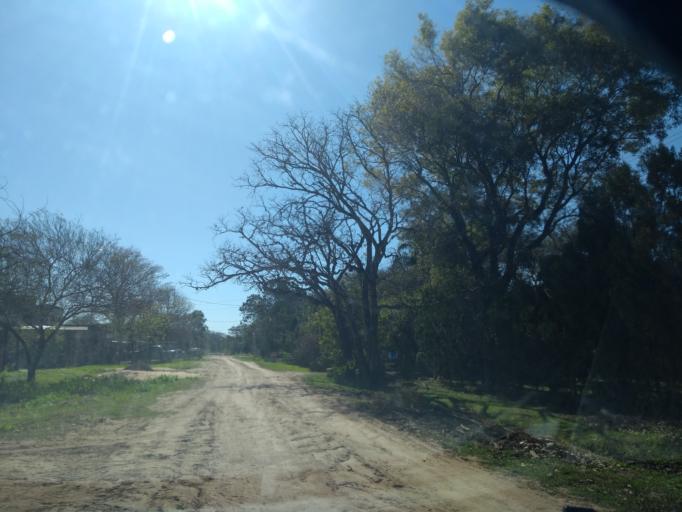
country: AR
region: Chaco
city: Resistencia
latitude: -27.4214
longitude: -58.9463
